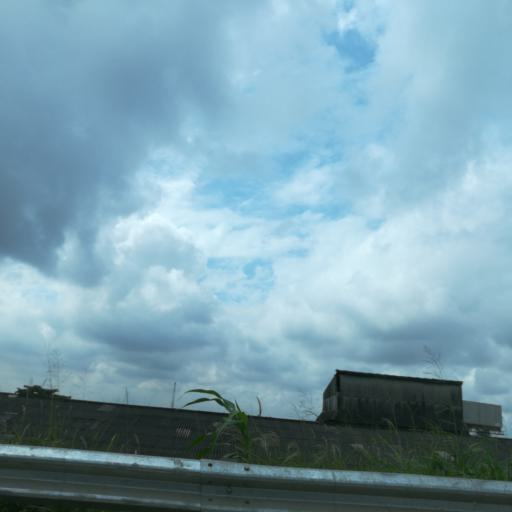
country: NG
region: Lagos
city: Ikeja
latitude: 6.5905
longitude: 3.3385
